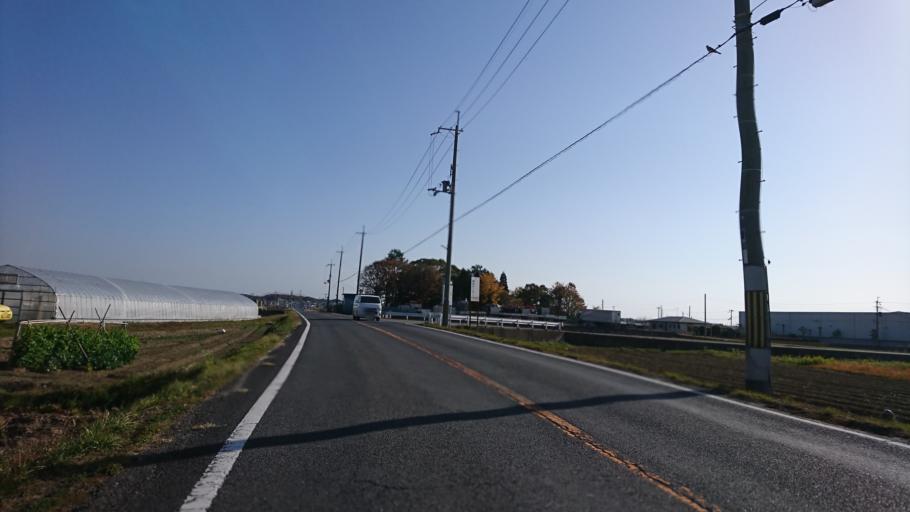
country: JP
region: Hyogo
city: Miki
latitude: 34.7607
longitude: 134.9294
